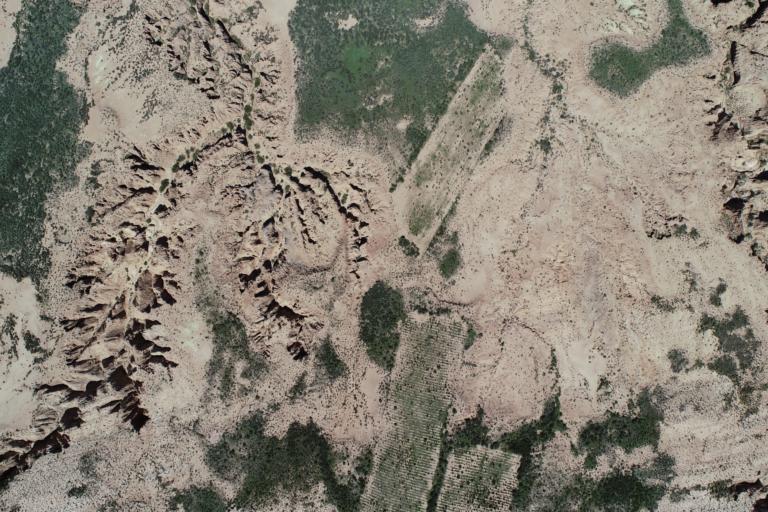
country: BO
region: La Paz
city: Patacamaya
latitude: -17.2924
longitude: -68.4940
